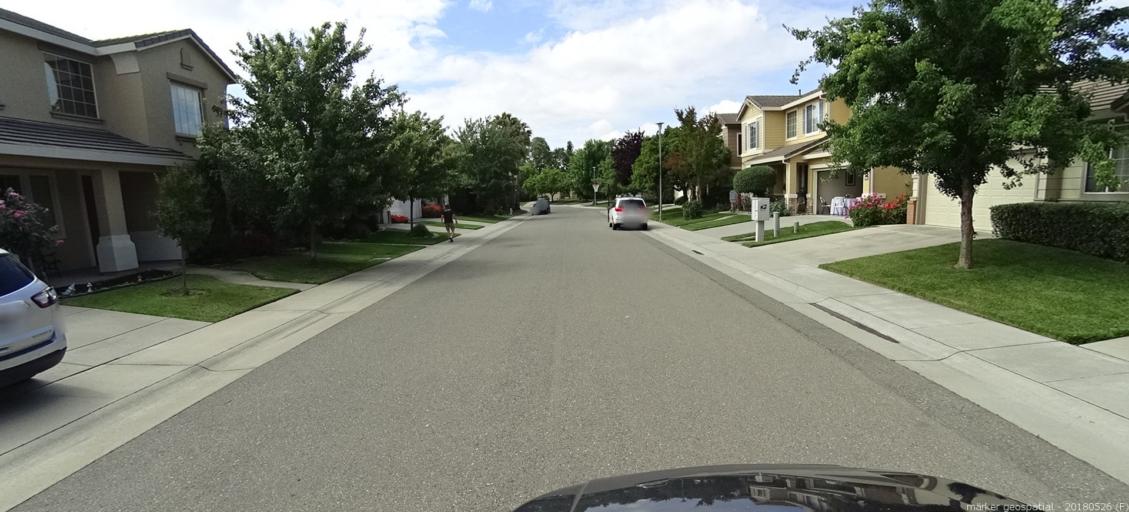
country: US
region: California
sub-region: Yolo County
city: West Sacramento
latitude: 38.6102
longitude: -121.5368
